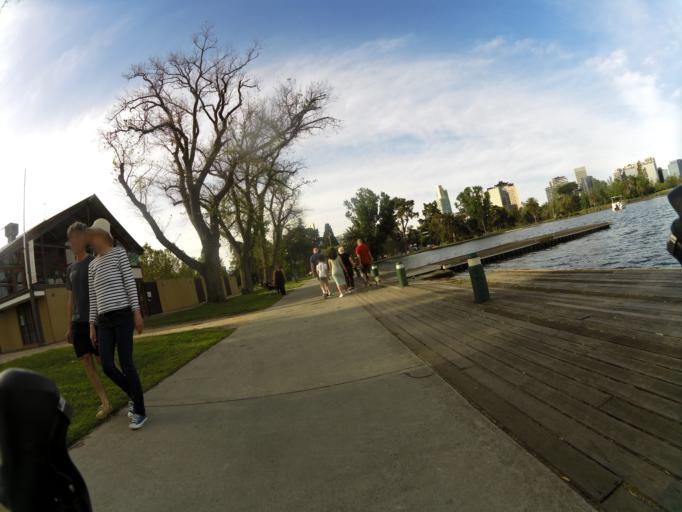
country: AU
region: Victoria
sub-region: Port Phillip
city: South Melbourne
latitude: -37.8400
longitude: 144.9672
